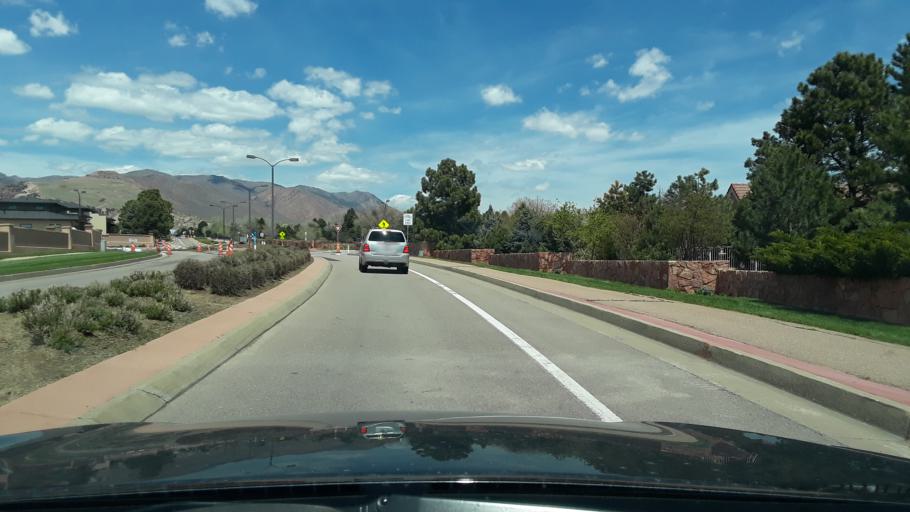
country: US
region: Colorado
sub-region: El Paso County
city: Manitou Springs
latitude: 38.8772
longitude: -104.8653
